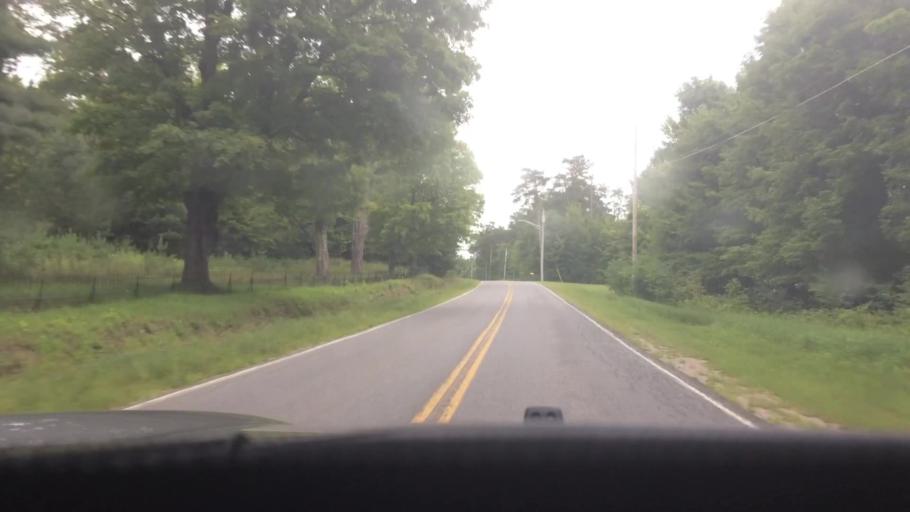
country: US
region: New York
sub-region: St. Lawrence County
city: Hannawa Falls
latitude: 44.5584
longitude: -74.9275
